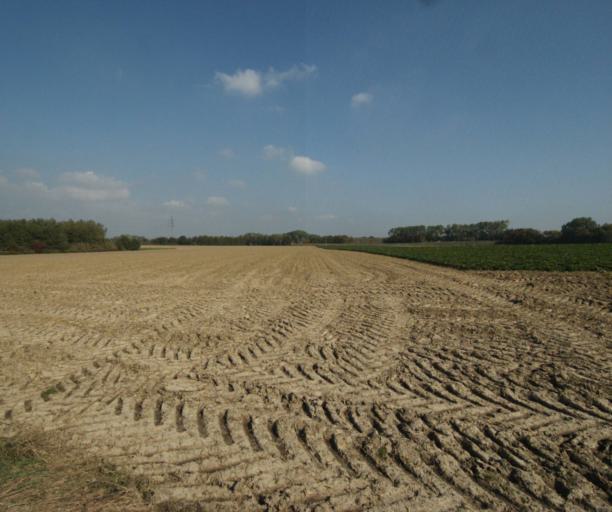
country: FR
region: Nord-Pas-de-Calais
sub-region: Departement du Nord
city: Attiches
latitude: 50.5359
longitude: 3.0457
